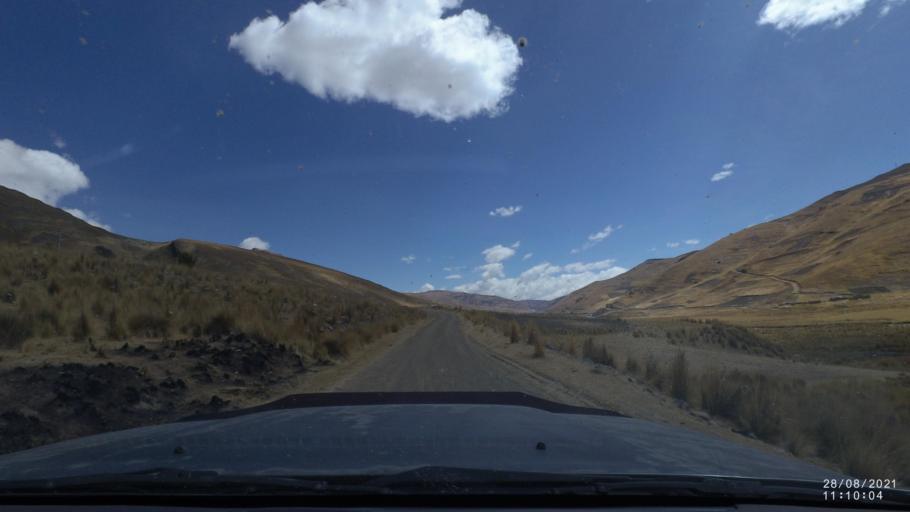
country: BO
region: Cochabamba
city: Cochabamba
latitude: -17.1582
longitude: -66.3097
